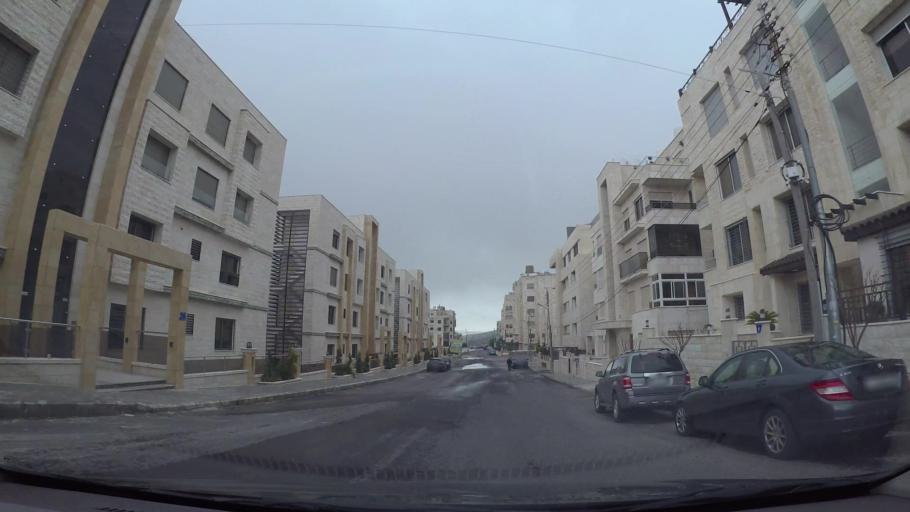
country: JO
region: Amman
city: Al Bunayyat ash Shamaliyah
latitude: 31.9381
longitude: 35.8695
